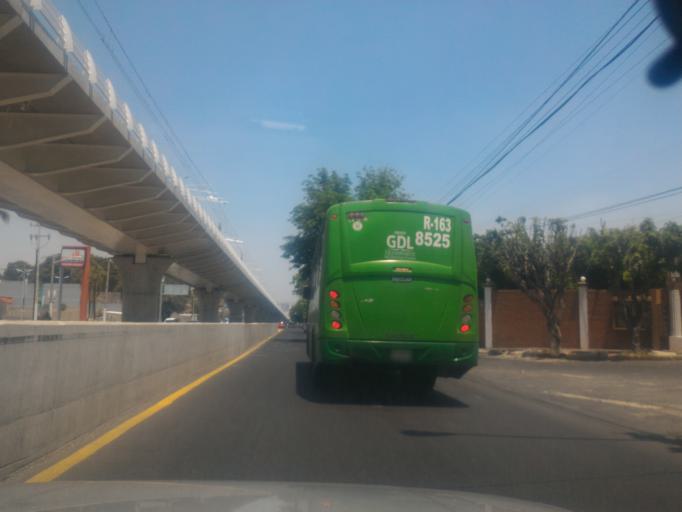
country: MX
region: Jalisco
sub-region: Zapopan
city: Zapopan
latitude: 20.7187
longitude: -103.3853
